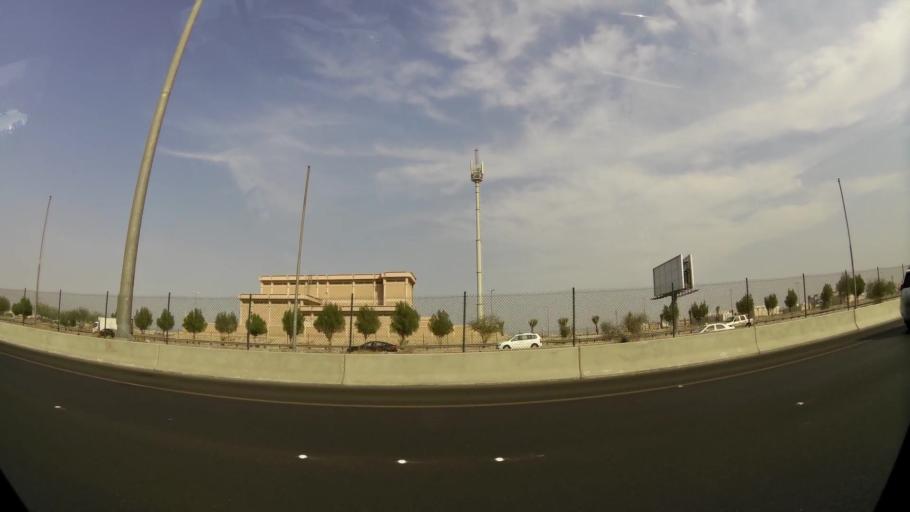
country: KW
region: Al Farwaniyah
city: Janub as Surrah
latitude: 29.2968
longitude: 47.9812
